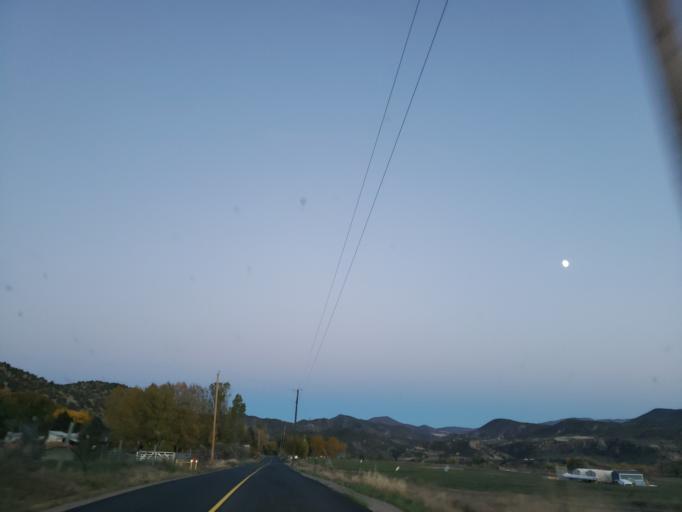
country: US
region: Colorado
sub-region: Garfield County
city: New Castle
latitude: 39.5604
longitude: -107.5729
